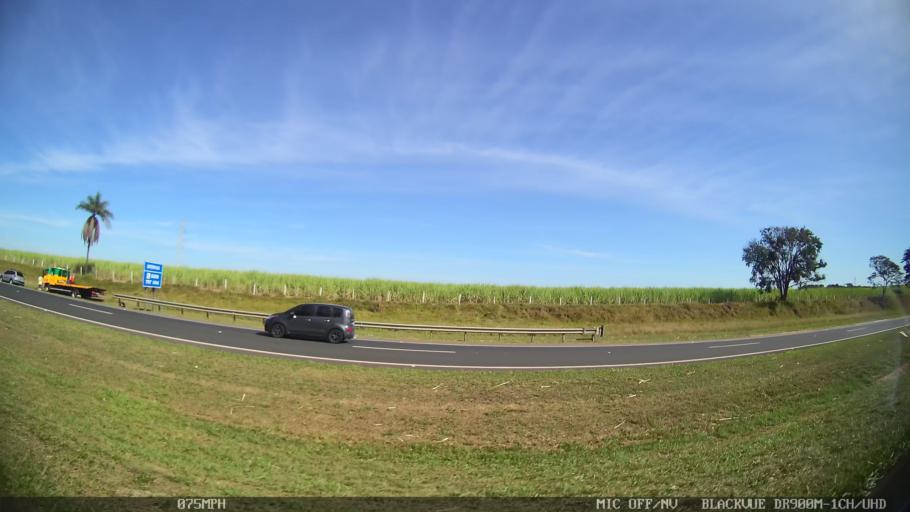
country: BR
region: Sao Paulo
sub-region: Porto Ferreira
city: Porto Ferreira
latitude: -21.8963
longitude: -47.4805
